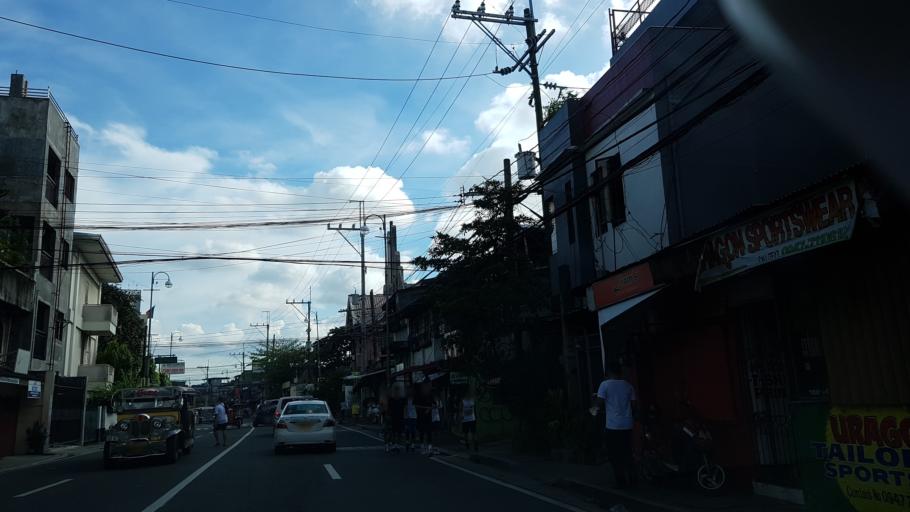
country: PH
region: Calabarzon
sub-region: Province of Rizal
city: Pateros
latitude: 14.5539
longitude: 121.0639
